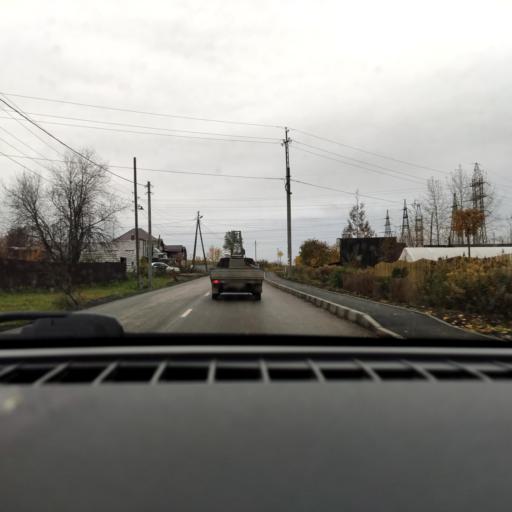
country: RU
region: Perm
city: Ferma
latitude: 57.9197
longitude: 56.3035
